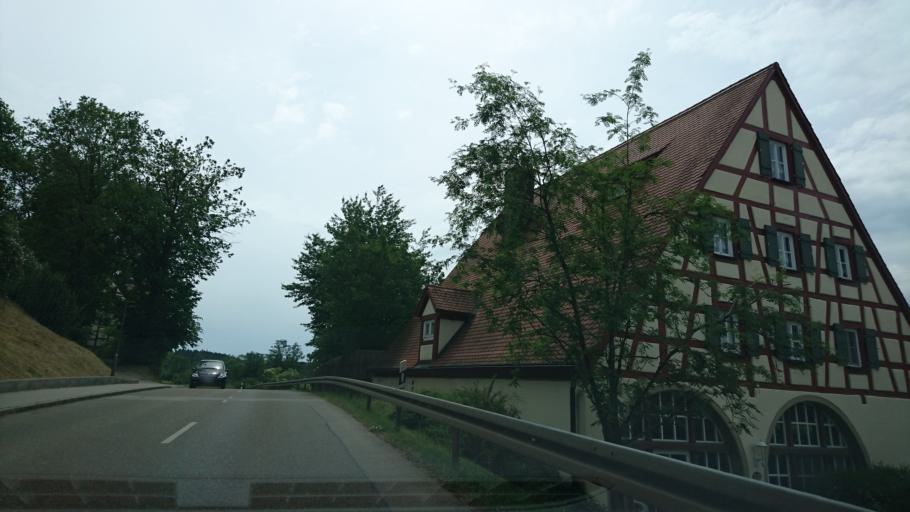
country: DE
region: Bavaria
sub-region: Regierungsbezirk Mittelfranken
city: Pleinfeld
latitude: 49.1004
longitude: 10.9851
